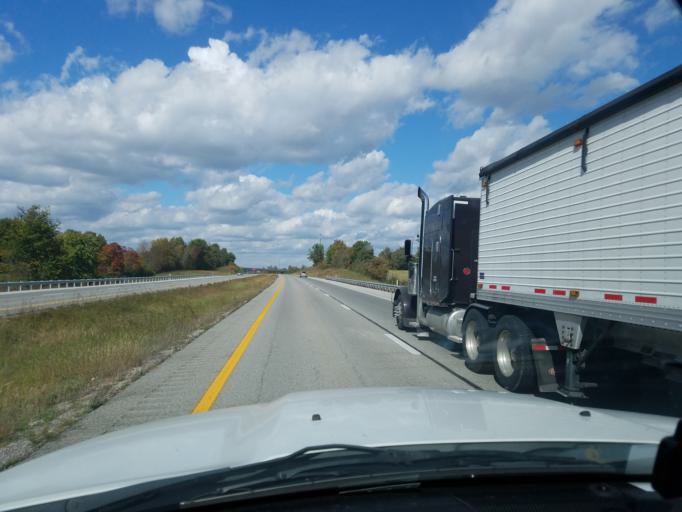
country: US
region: Kentucky
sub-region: Daviess County
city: Masonville
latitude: 37.6934
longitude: -87.0356
